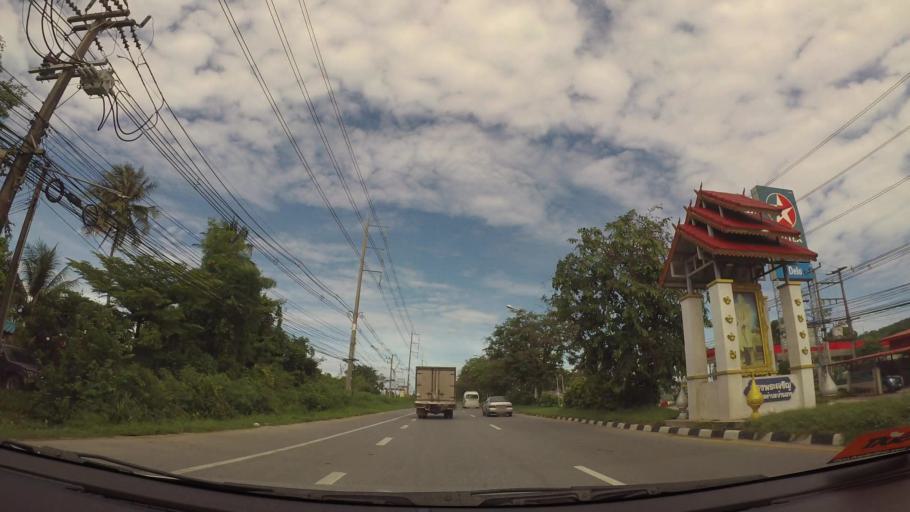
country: TH
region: Rayong
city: Ban Chang
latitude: 12.7464
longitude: 101.0992
